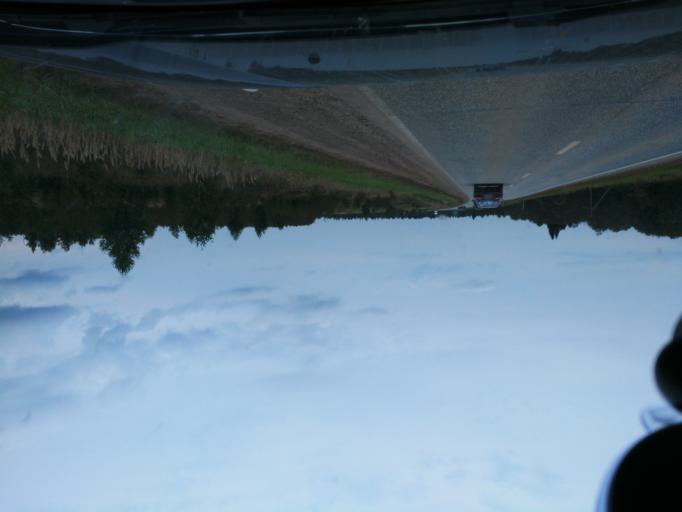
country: RU
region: Perm
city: Chernushka
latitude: 56.5221
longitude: 56.0196
